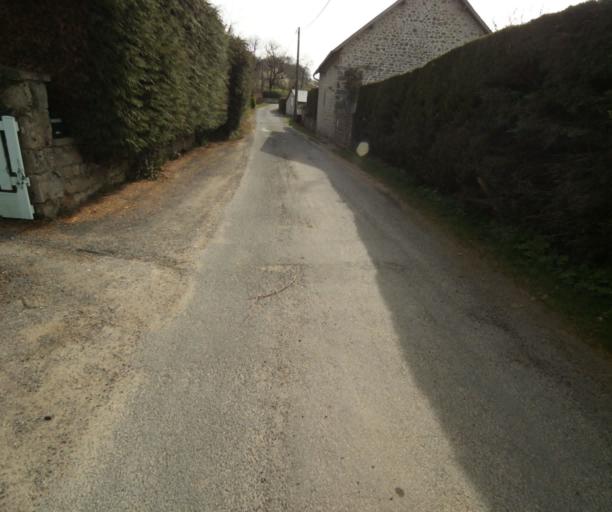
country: FR
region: Limousin
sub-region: Departement de la Correze
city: Correze
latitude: 45.4116
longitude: 1.8274
